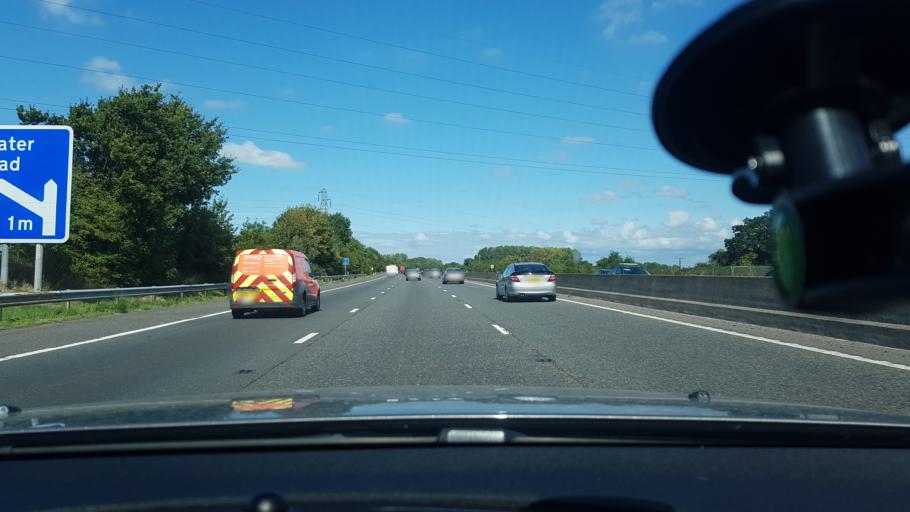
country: GB
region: England
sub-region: Somerset
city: North Petherton
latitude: 51.0839
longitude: -3.0062
